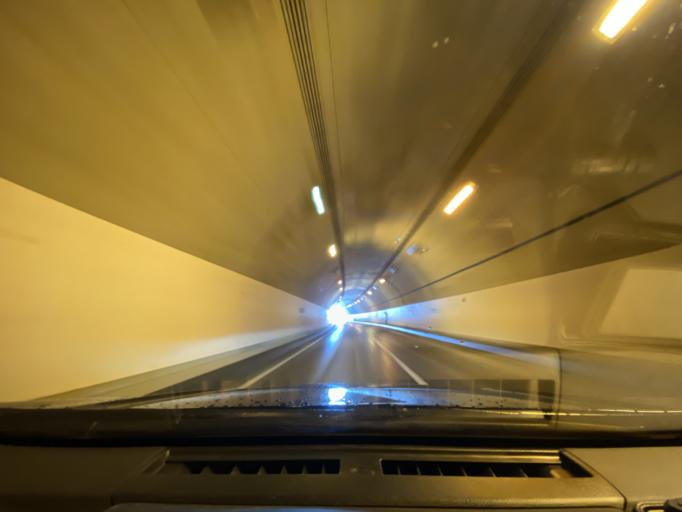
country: JP
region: Hokkaido
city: Ishikari
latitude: 43.4736
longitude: 141.3928
